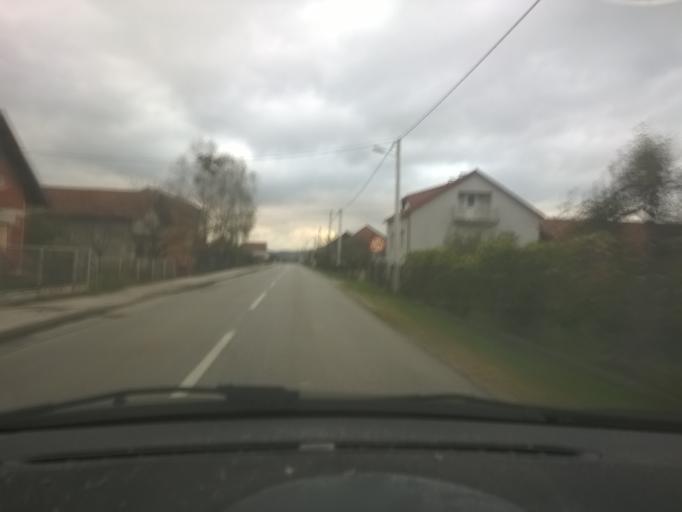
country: HR
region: Zagrebacka
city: Jakovlje
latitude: 45.9826
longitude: 15.8383
